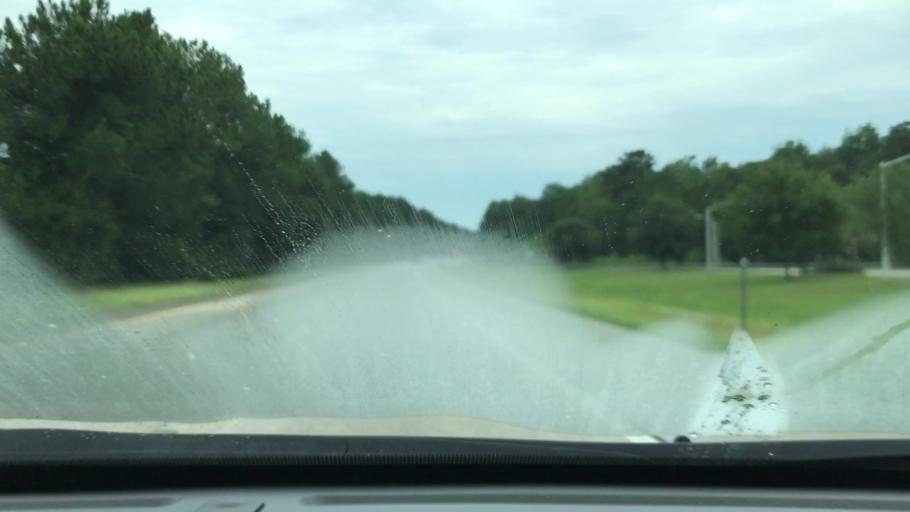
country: US
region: South Carolina
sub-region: Hampton County
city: Yemassee
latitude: 32.7986
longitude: -80.7728
